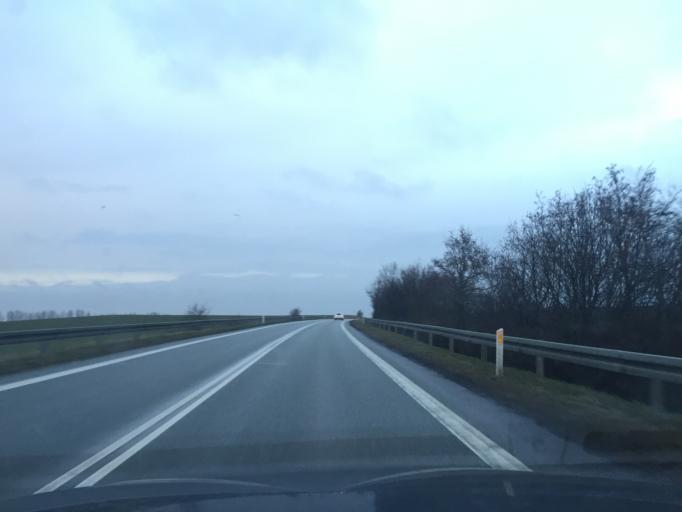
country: DK
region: Zealand
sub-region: Slagelse Kommune
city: Slagelse
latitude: 55.3750
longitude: 11.3294
